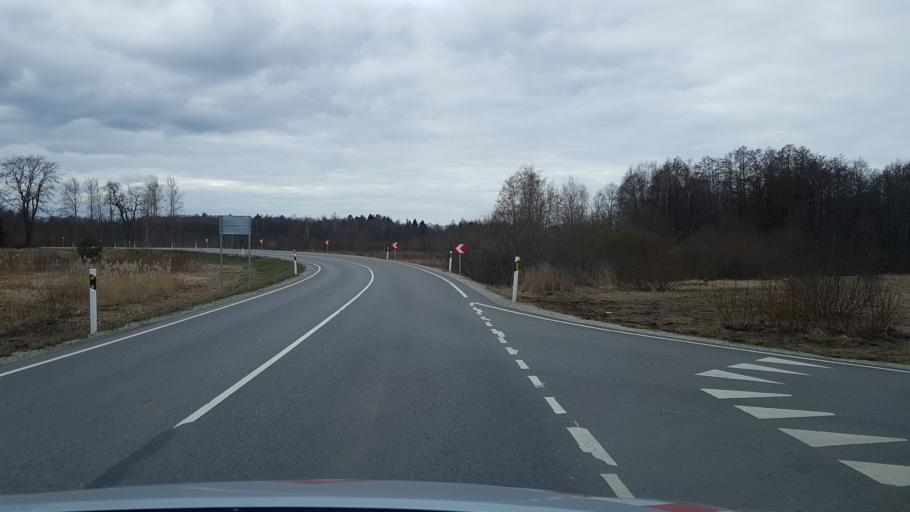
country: EE
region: Ida-Virumaa
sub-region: Narva-Joesuu linn
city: Narva-Joesuu
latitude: 59.4119
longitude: 28.0712
